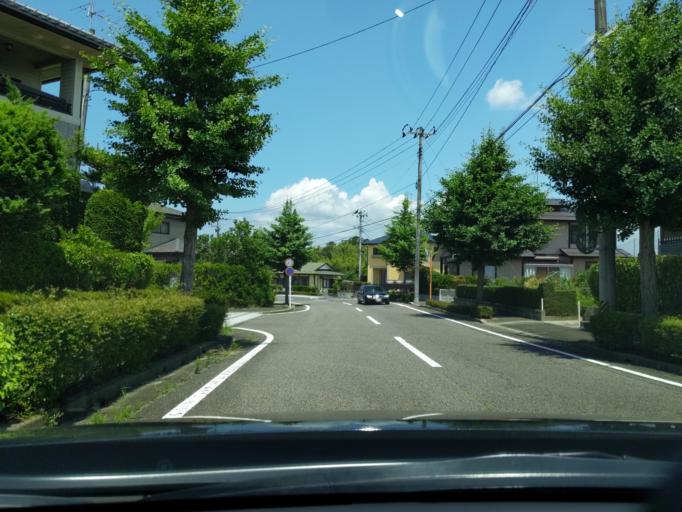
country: JP
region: Fukushima
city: Sukagawa
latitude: 37.3414
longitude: 140.3493
